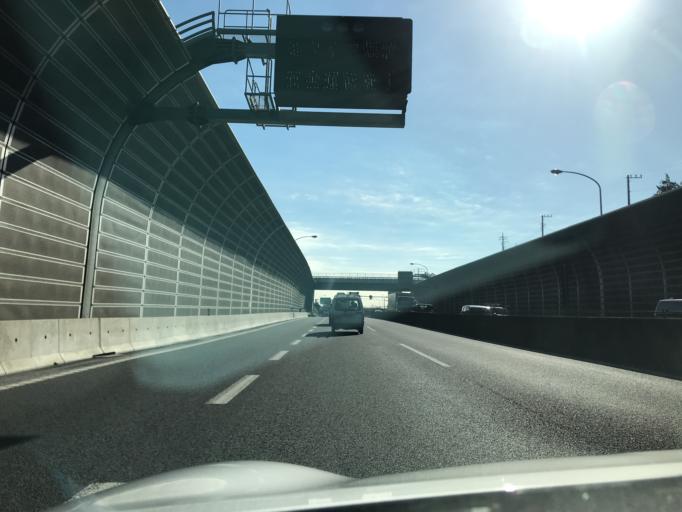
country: JP
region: Chiba
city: Chiba
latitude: 35.6265
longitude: 140.1376
